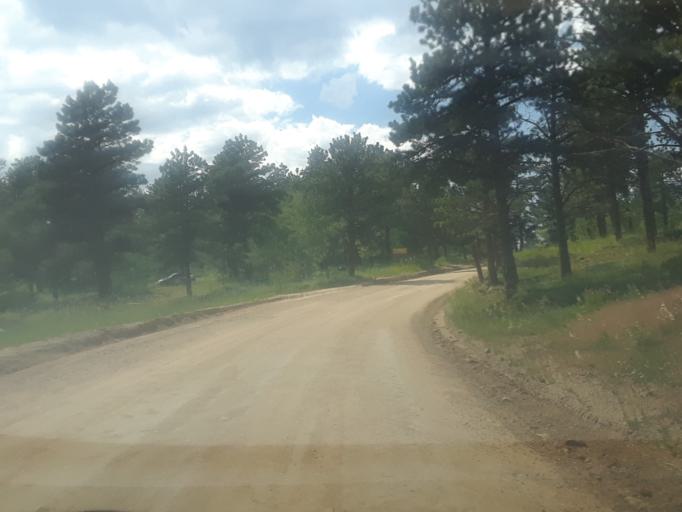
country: US
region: Colorado
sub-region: Boulder County
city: Nederland
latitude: 40.0584
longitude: -105.4287
